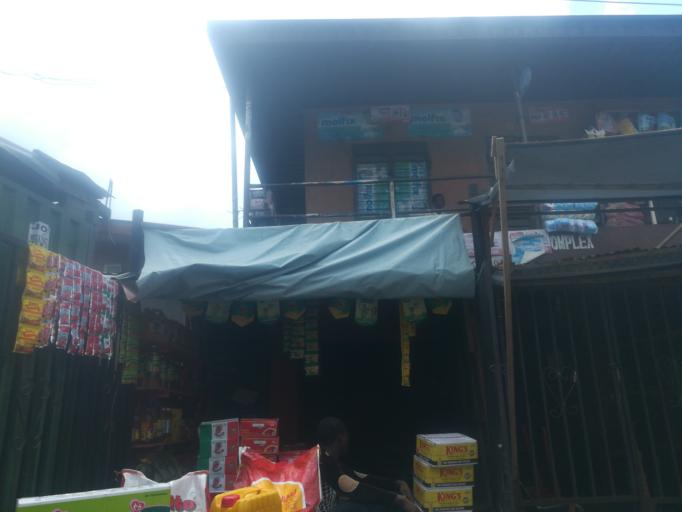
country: NG
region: Lagos
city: Ojota
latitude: 6.5991
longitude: 3.3885
